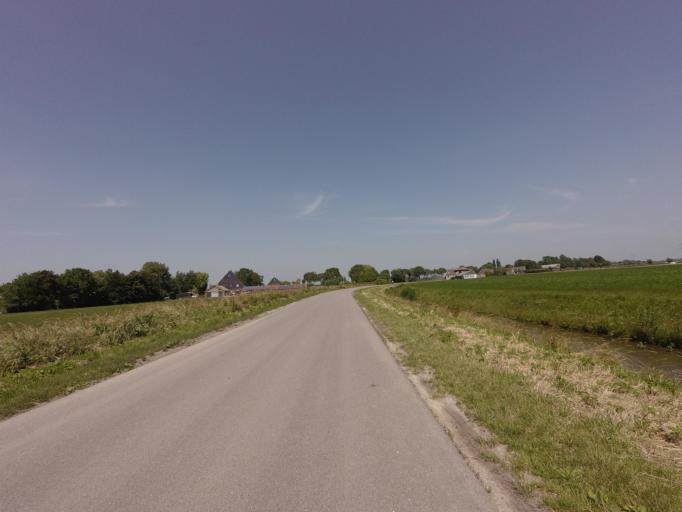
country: NL
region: North Holland
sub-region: Gemeente Opmeer
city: Opmeer
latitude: 52.6466
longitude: 4.9625
